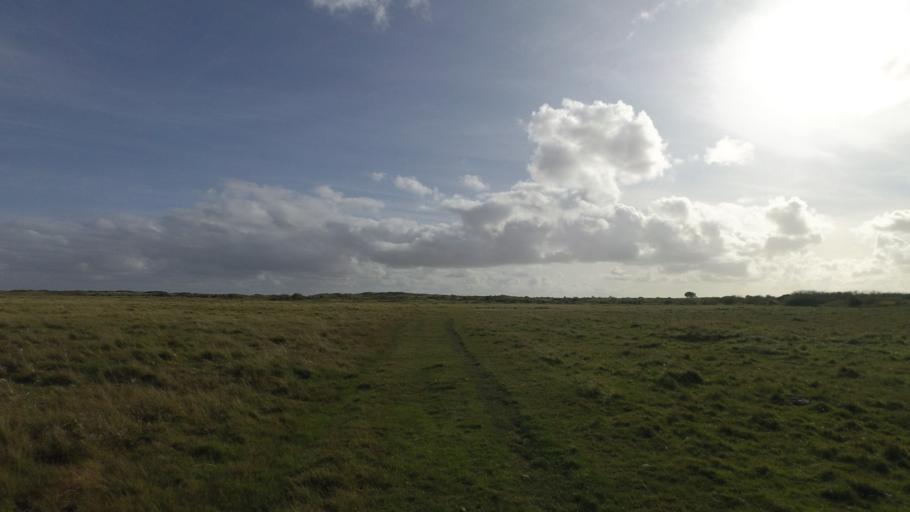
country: NL
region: Friesland
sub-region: Gemeente Ameland
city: Nes
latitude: 53.4597
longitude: 5.8362
